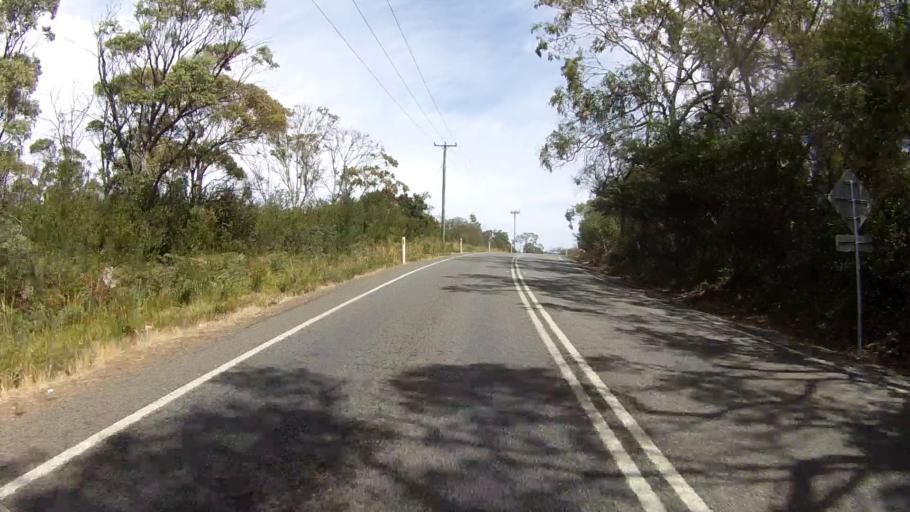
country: AU
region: Tasmania
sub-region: Clarence
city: Sandford
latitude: -43.0256
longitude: 147.4825
